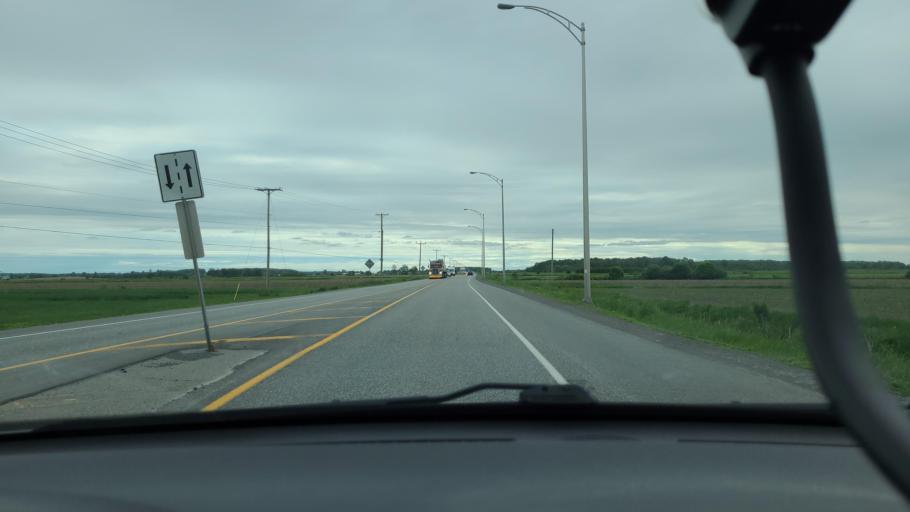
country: CA
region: Quebec
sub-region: Lanaudiere
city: Sainte-Julienne
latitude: 45.9125
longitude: -73.6543
